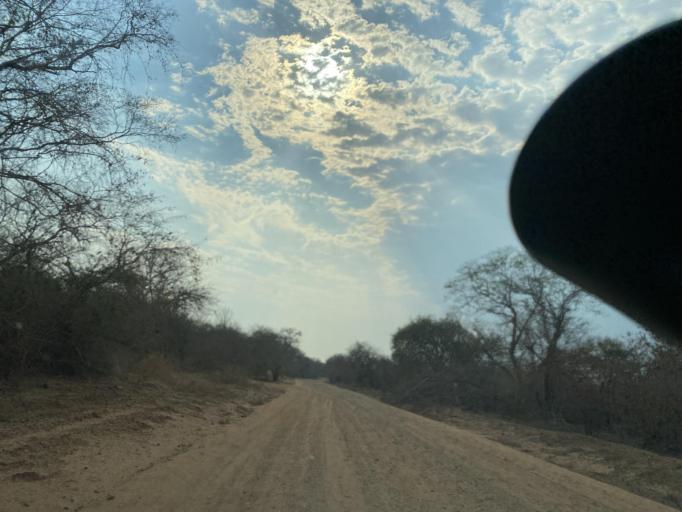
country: ZW
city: Chirundu
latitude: -15.9306
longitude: 28.9231
